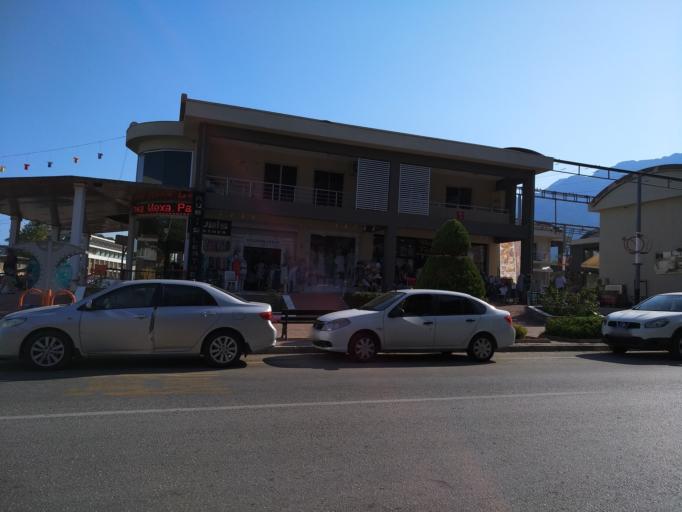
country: TR
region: Antalya
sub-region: Kemer
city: Goeynuek
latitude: 36.6648
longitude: 30.5572
